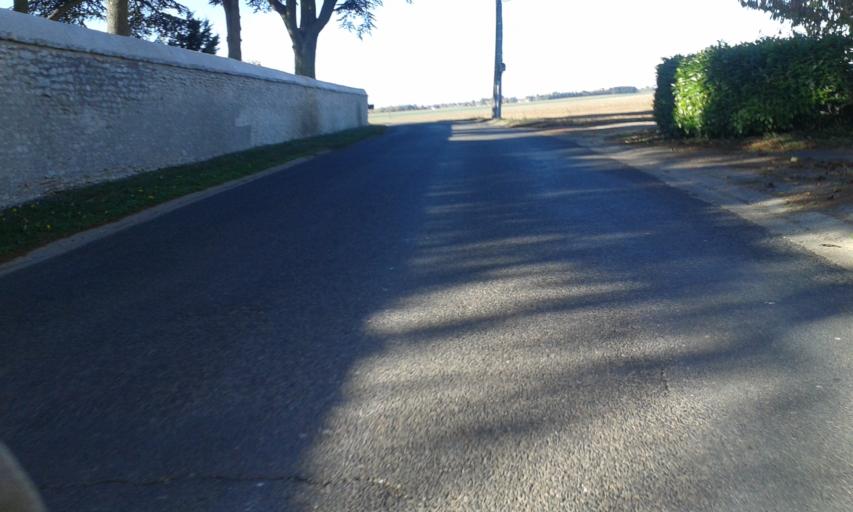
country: FR
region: Centre
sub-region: Departement du Loiret
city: Tavers
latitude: 47.7780
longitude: 1.5454
